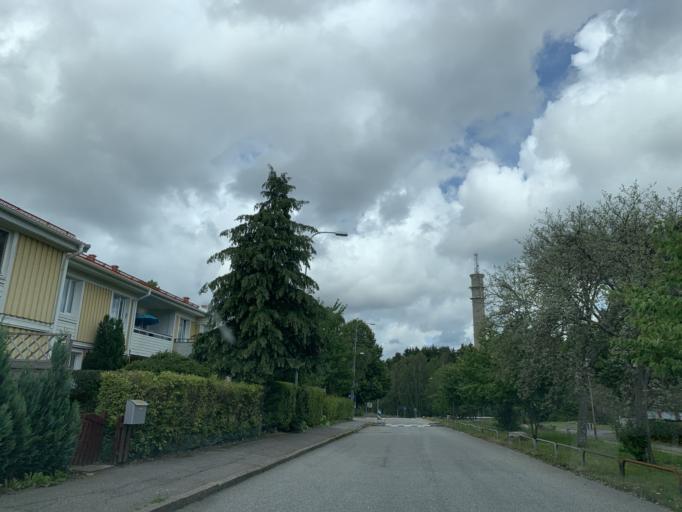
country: SE
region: Vaestra Goetaland
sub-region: Goteborg
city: Eriksbo
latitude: 57.7613
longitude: 12.0681
